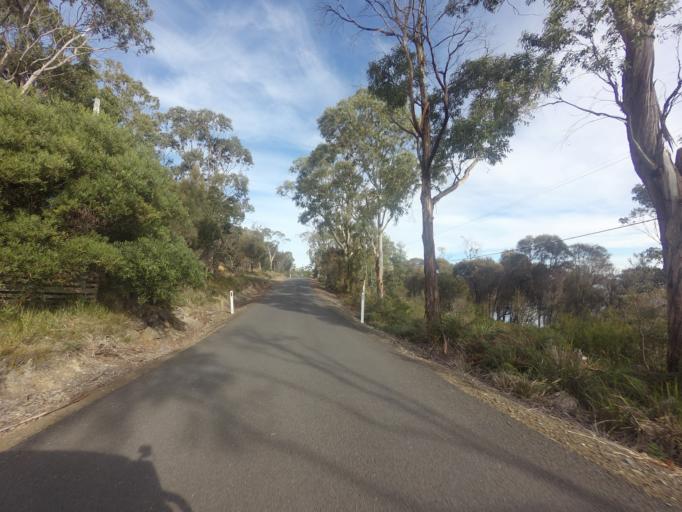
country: AU
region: Tasmania
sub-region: Sorell
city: Sorell
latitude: -42.9760
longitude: 147.8370
